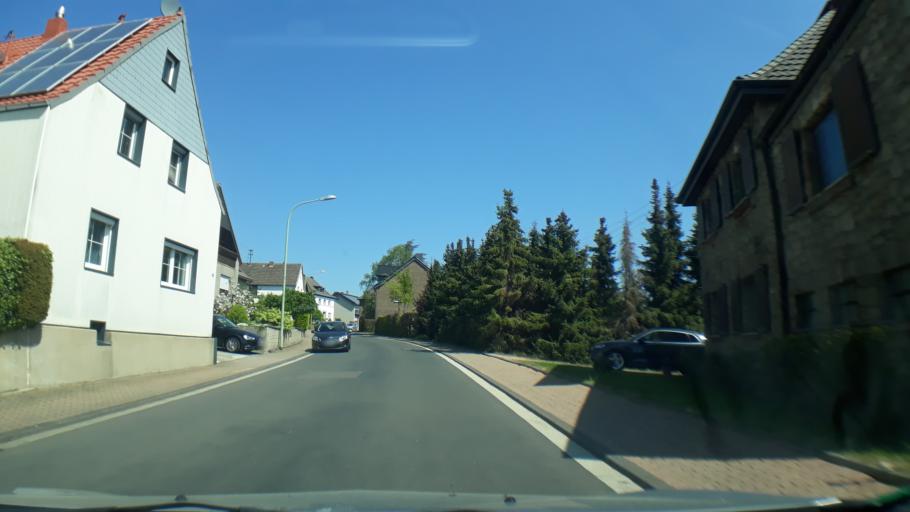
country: DE
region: North Rhine-Westphalia
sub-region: Regierungsbezirk Koln
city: Nideggen
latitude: 50.6947
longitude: 6.4328
